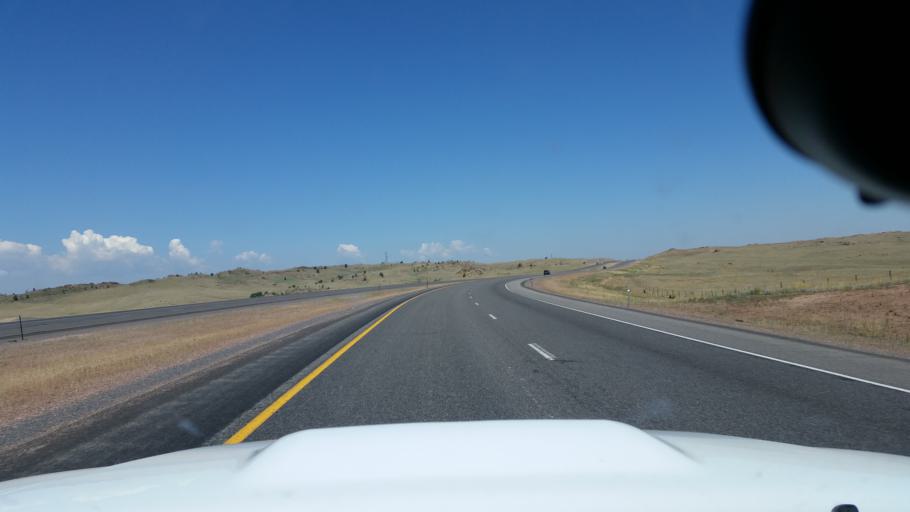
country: US
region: Wyoming
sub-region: Albany County
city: Laramie
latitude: 41.0436
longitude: -105.4597
